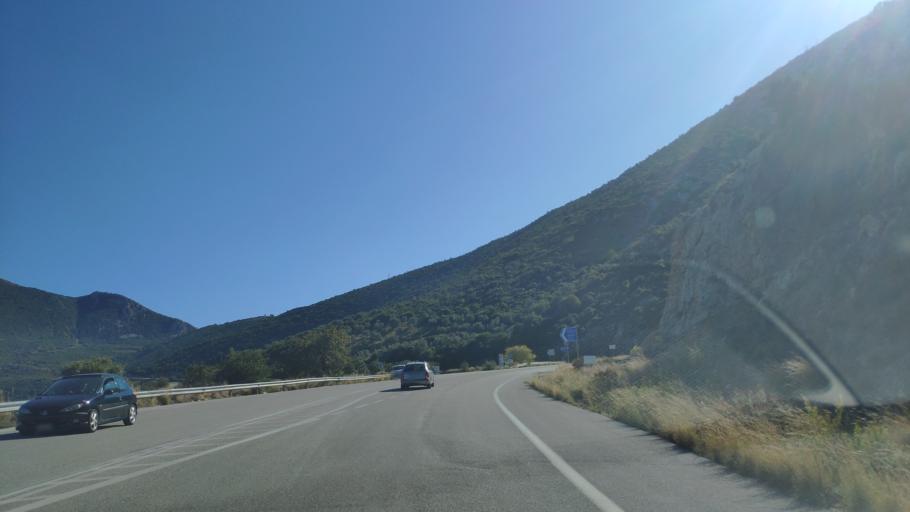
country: GR
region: Peloponnese
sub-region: Nomos Argolidos
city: Palaia Epidavros
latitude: 37.6127
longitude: 23.1519
